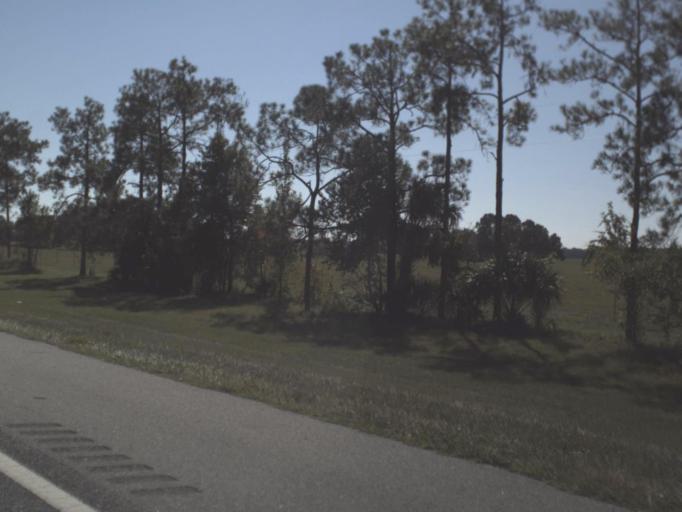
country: US
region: Florida
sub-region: Sumter County
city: Wildwood
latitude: 28.7918
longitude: -81.9910
